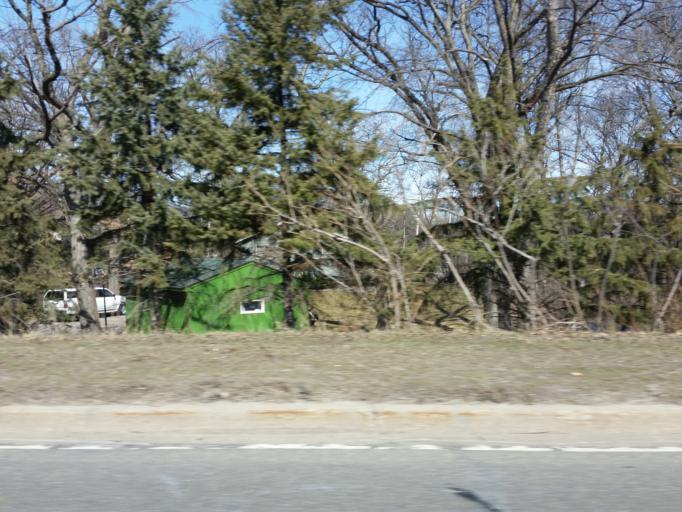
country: US
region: Minnesota
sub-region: Dakota County
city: Eagan
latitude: 44.7902
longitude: -93.1928
